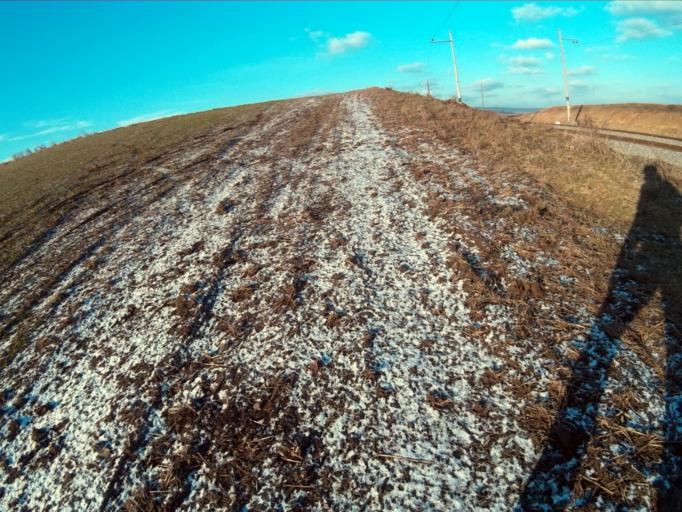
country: CZ
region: South Moravian
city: Krenovice
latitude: 49.1616
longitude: 16.8147
